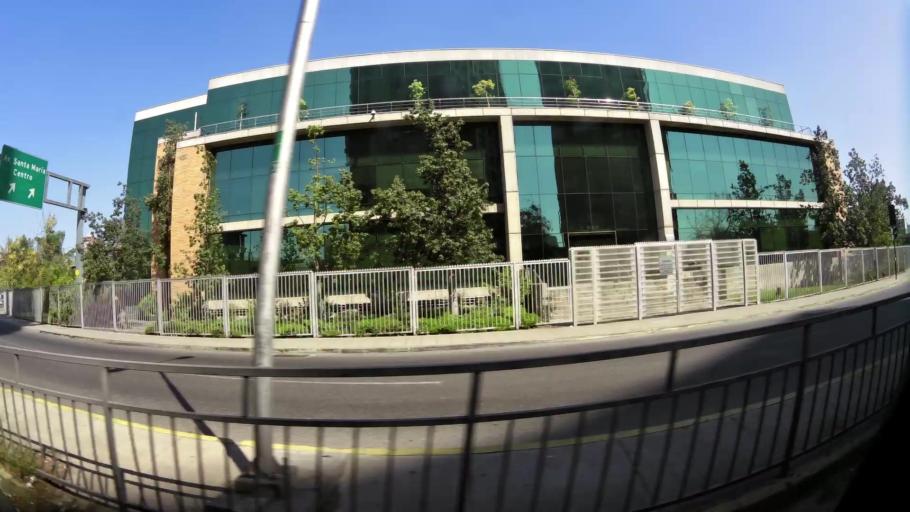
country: CL
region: Santiago Metropolitan
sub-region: Provincia de Santiago
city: Santiago
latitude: -33.4297
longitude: -70.6578
